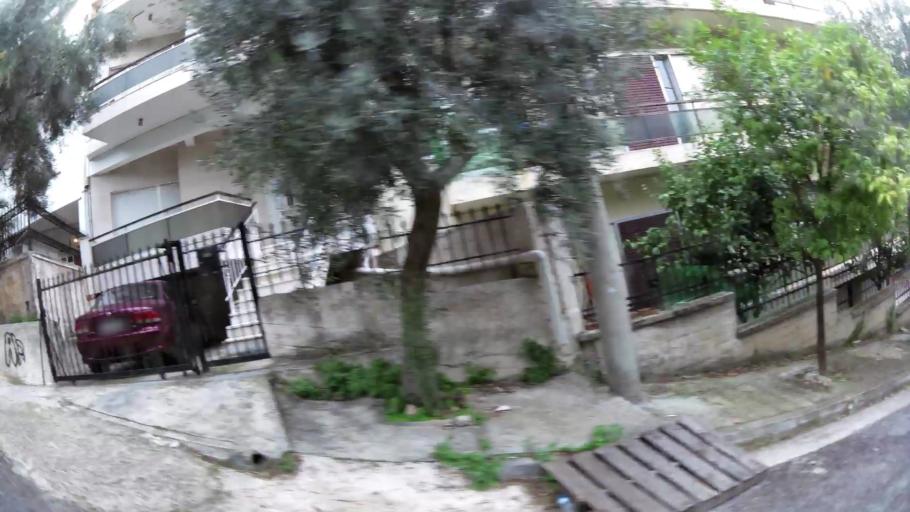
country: GR
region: Attica
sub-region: Nomarchia Athinas
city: Kaisariani
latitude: 37.9614
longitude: 23.7645
